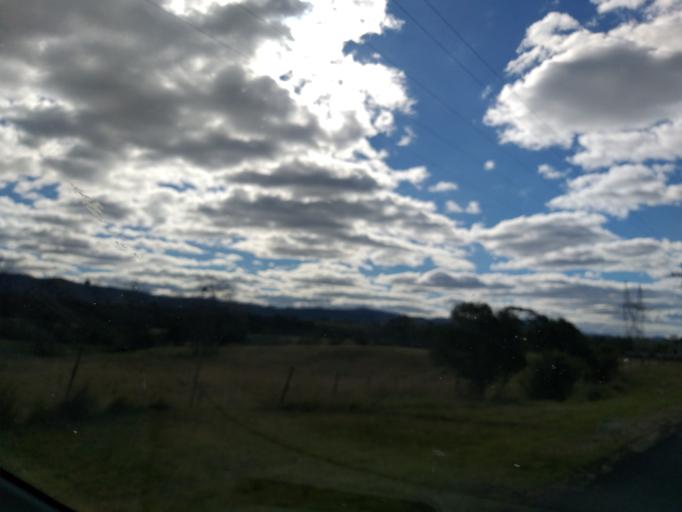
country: AU
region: New South Wales
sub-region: Wollongong
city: Dapto
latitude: -34.5318
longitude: 150.7713
